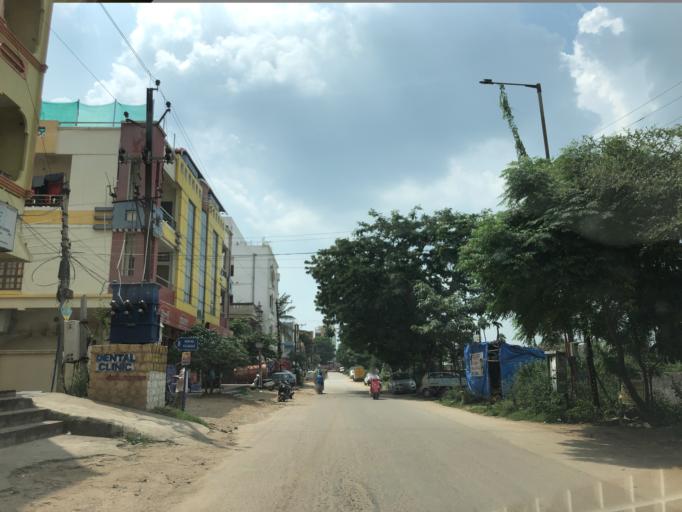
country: IN
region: Telangana
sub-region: Rangareddi
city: Quthbullapur
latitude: 17.4822
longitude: 78.4779
